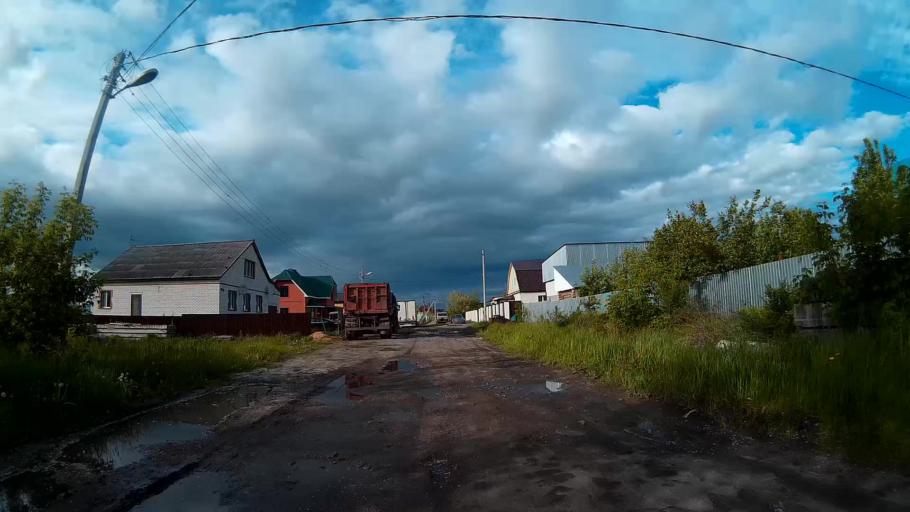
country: RU
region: Ulyanovsk
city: Novoul'yanovsk
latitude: 54.2007
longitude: 48.2725
